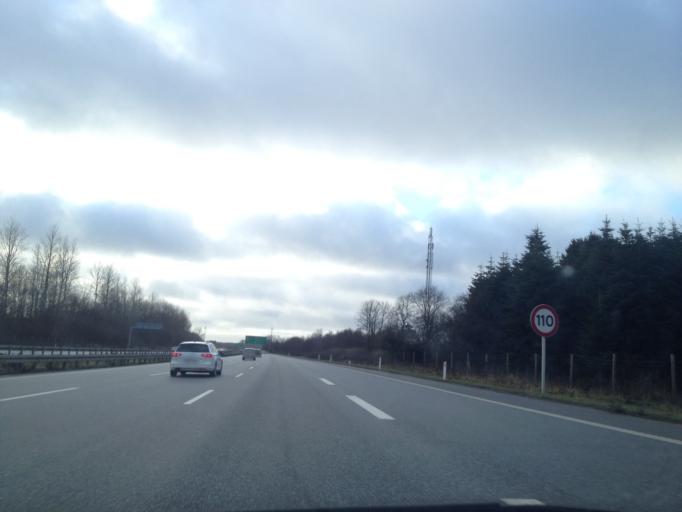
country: DK
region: Capital Region
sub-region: Albertslund Kommune
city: Albertslund
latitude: 55.6803
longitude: 12.3295
